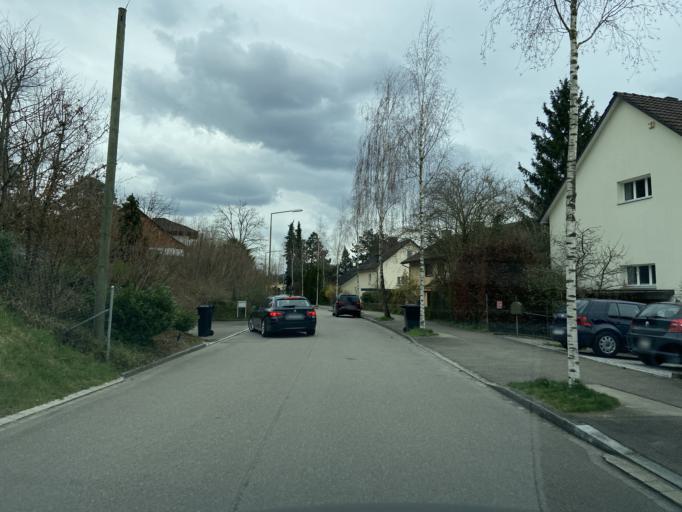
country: CH
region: Zurich
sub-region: Bezirk Winterthur
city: Wuelflingen (Kreis 6) / Lindenplatz
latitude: 47.5133
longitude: 8.7016
